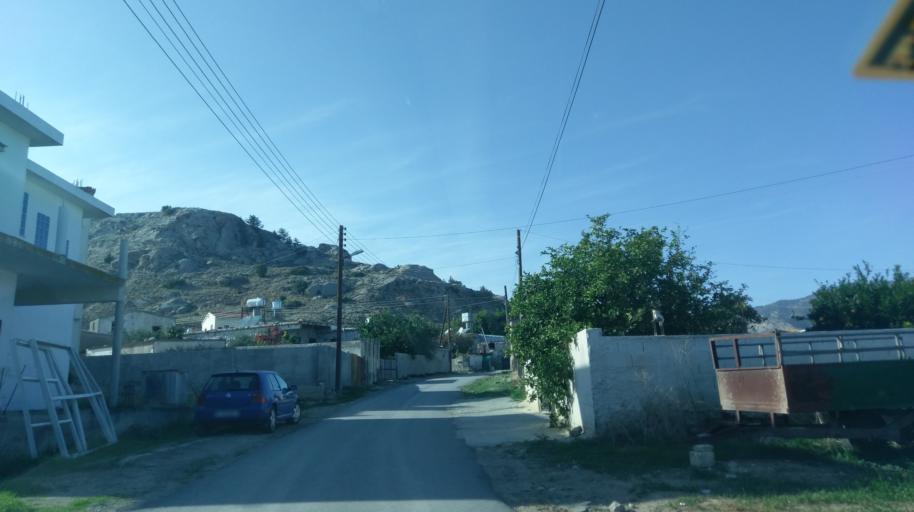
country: CY
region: Ammochostos
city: Trikomo
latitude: 35.3271
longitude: 33.8137
